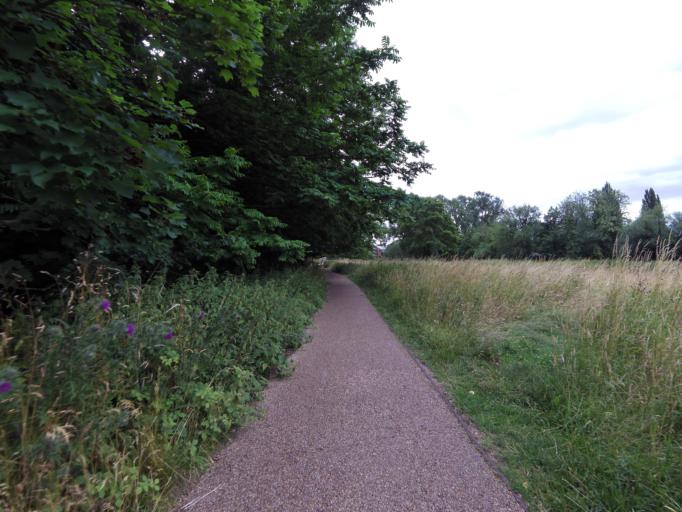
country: GB
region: England
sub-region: Cambridgeshire
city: Cambridge
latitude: 52.1986
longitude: 0.1189
